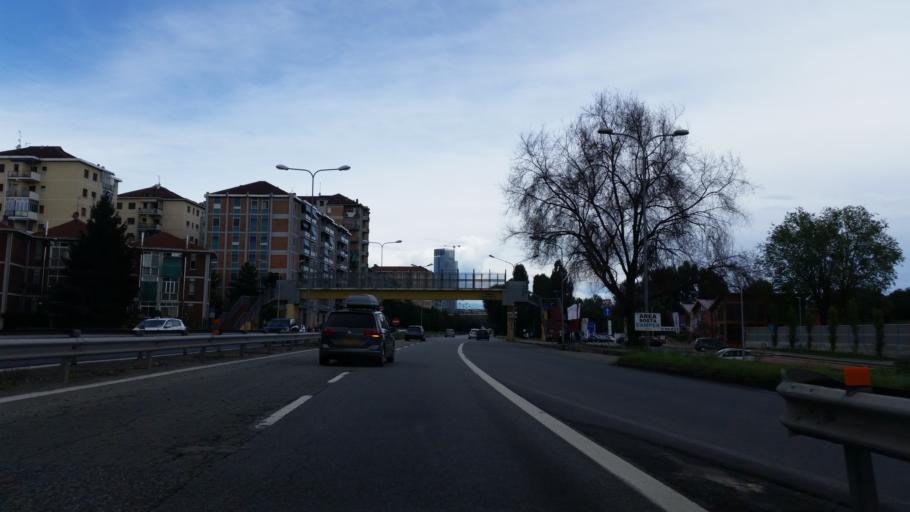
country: IT
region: Piedmont
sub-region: Provincia di Torino
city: Moncalieri
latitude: 45.0085
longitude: 7.6718
